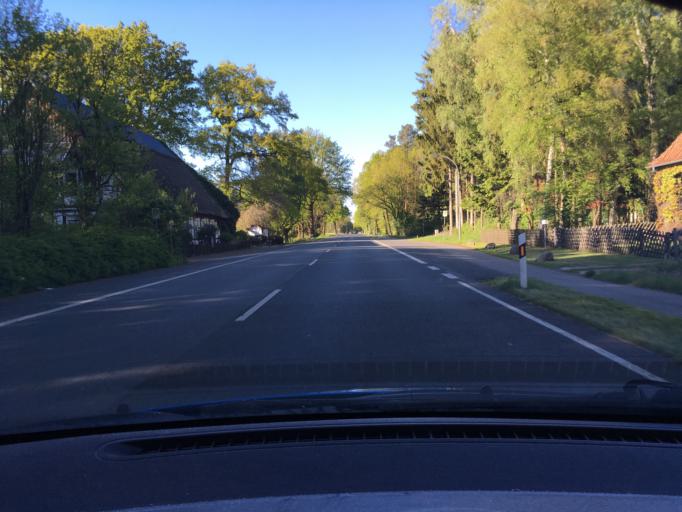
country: DE
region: Lower Saxony
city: Soltau
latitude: 53.0394
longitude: 9.8548
